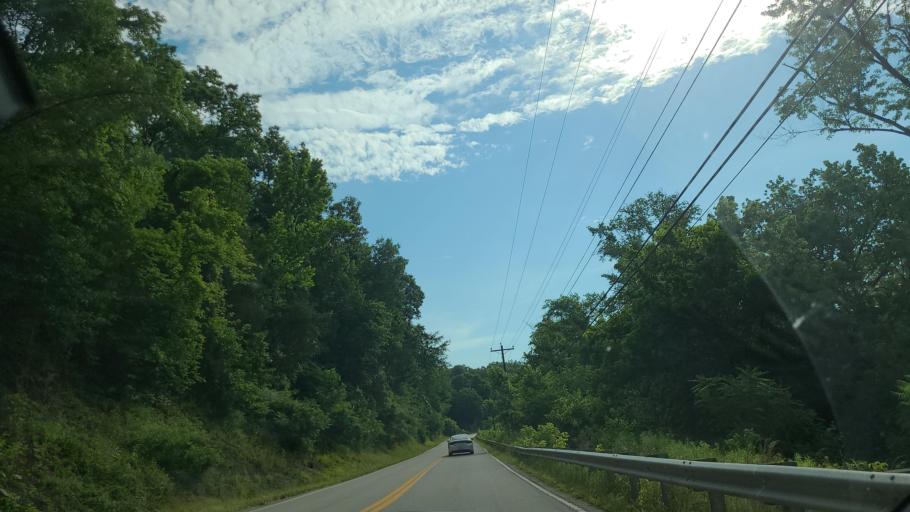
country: US
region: Kentucky
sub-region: Whitley County
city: Williamsburg
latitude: 36.7408
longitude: -84.0788
